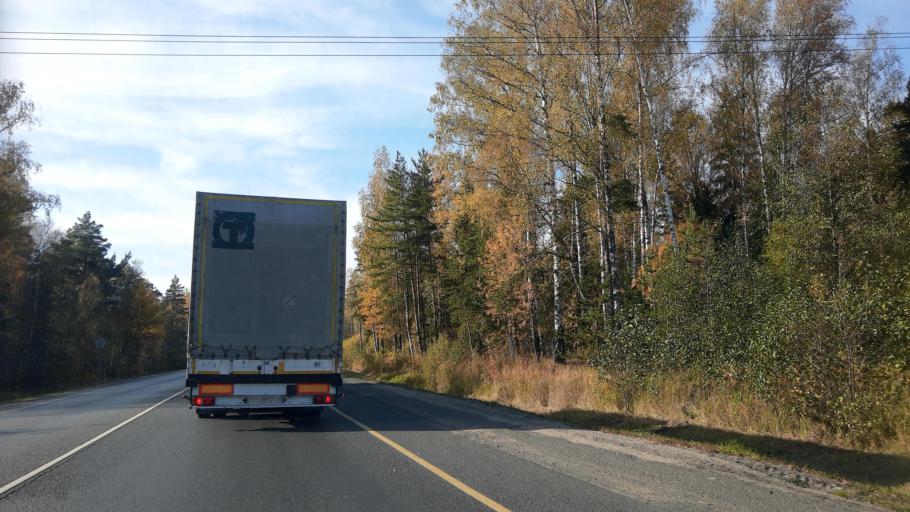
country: RU
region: Moskovskaya
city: Fryazevo
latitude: 55.7264
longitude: 38.4235
